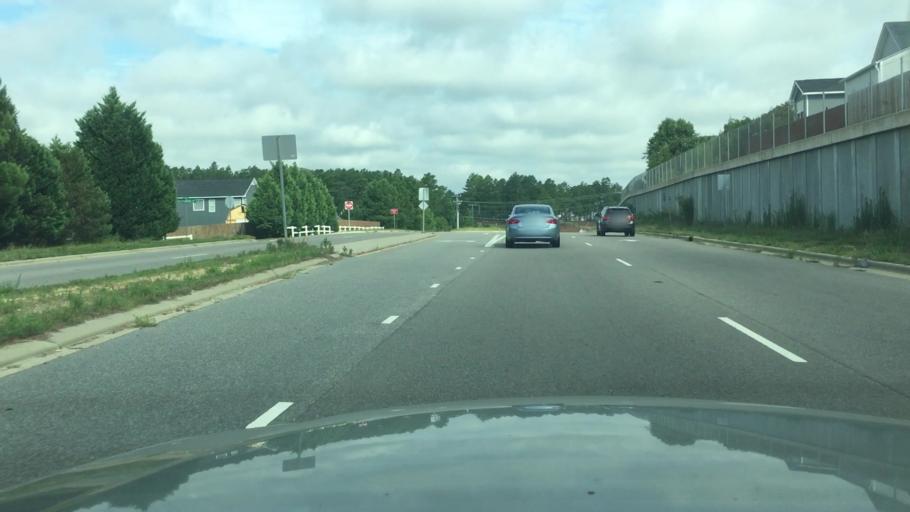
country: US
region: North Carolina
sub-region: Cumberland County
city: Hope Mills
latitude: 34.9723
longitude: -78.9186
